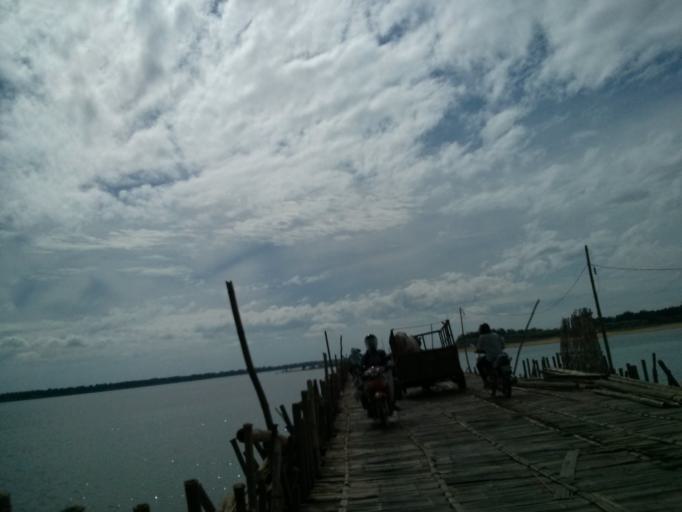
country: KH
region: Kampong Cham
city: Kampong Cham
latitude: 11.9763
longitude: 105.4617
